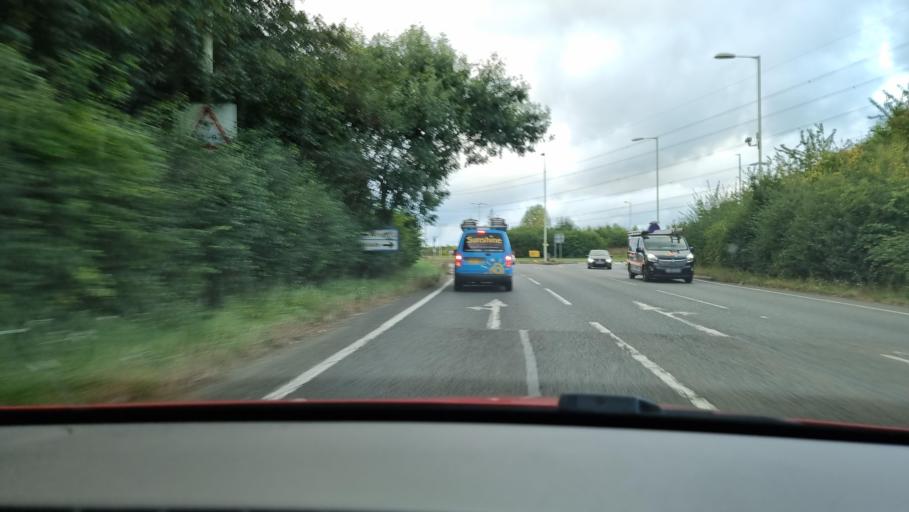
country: GB
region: England
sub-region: Central Bedfordshire
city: Leighton Buzzard
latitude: 51.9054
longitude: -0.6900
